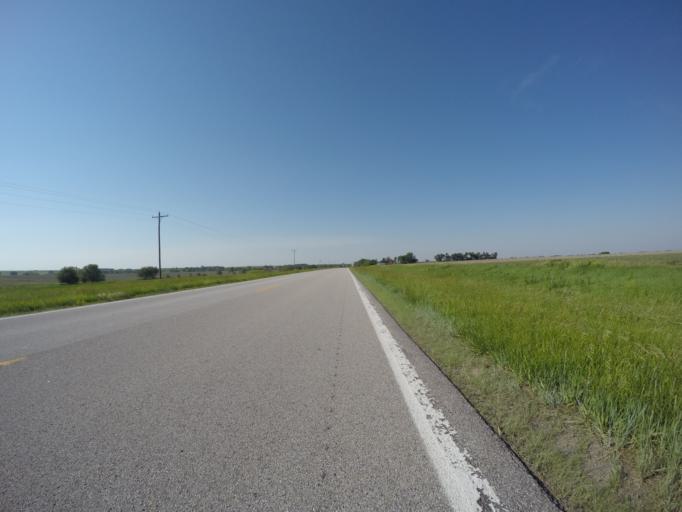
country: US
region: Nebraska
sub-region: Gage County
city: Wymore
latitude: 40.0526
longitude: -96.4829
